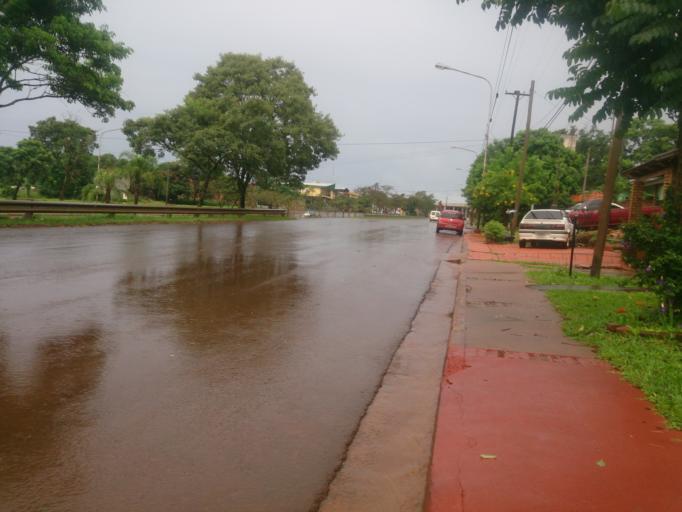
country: AR
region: Misiones
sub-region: Departamento de Obera
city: Obera
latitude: -27.4769
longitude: -55.0989
